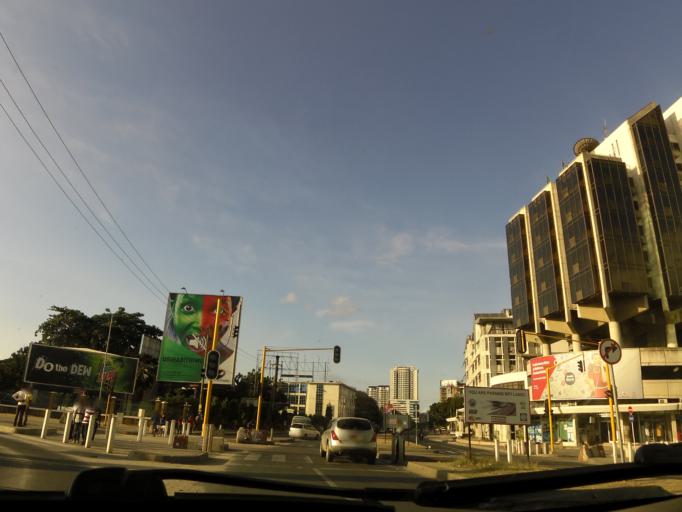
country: TZ
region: Dar es Salaam
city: Dar es Salaam
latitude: -6.8164
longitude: 39.2801
